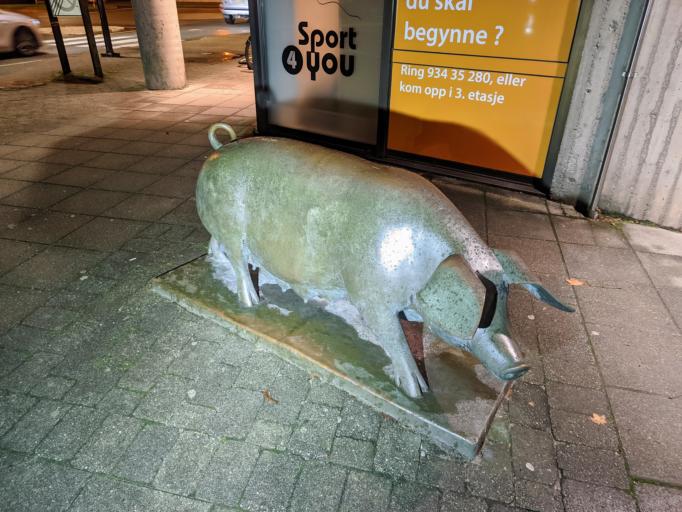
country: NO
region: Rogaland
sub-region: Time
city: Bryne
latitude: 58.7357
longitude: 5.6491
